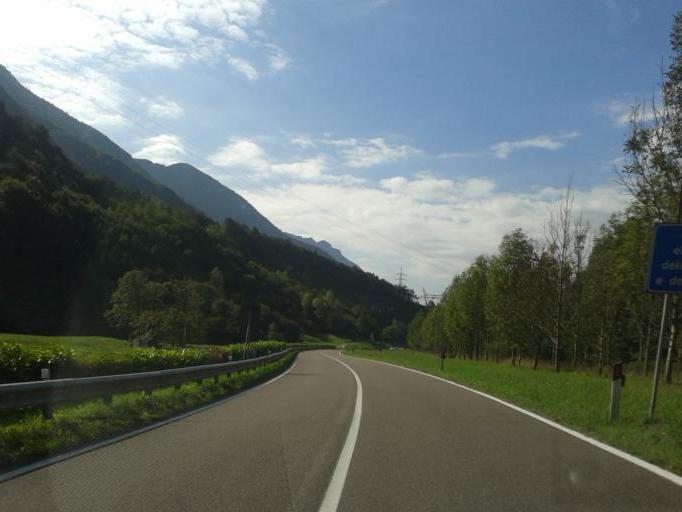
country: IT
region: Trentino-Alto Adige
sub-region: Provincia di Trento
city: Prezzo
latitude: 45.9269
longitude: 10.6344
